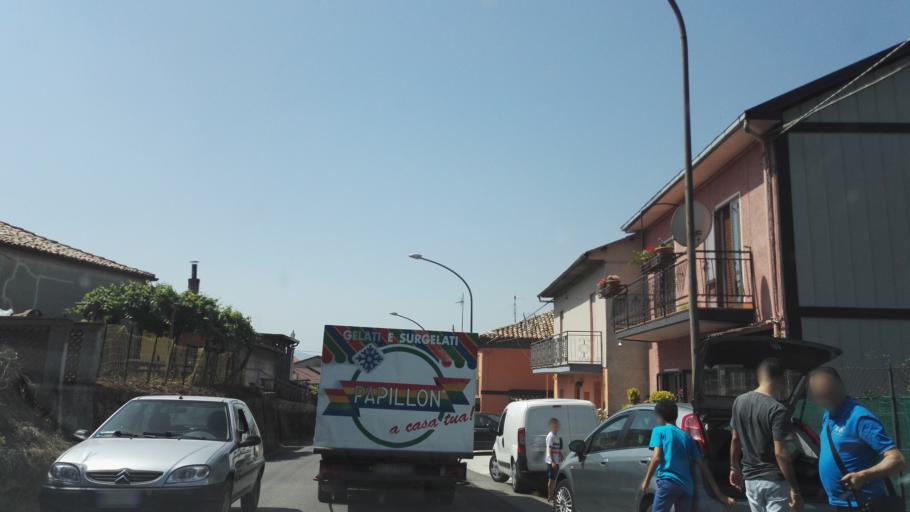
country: IT
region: Calabria
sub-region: Provincia di Vibo-Valentia
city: Mongiana
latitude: 38.5166
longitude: 16.3208
